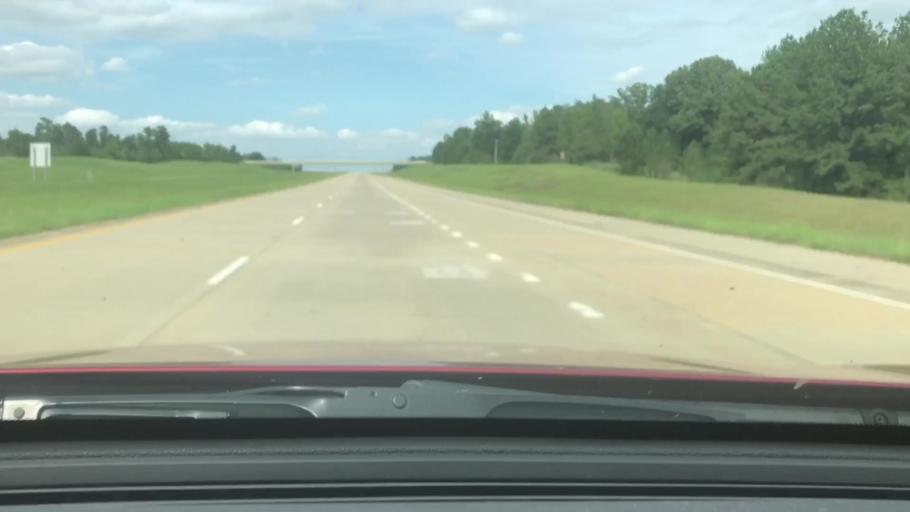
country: US
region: Louisiana
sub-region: Caddo Parish
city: Vivian
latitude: 33.0025
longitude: -93.9069
